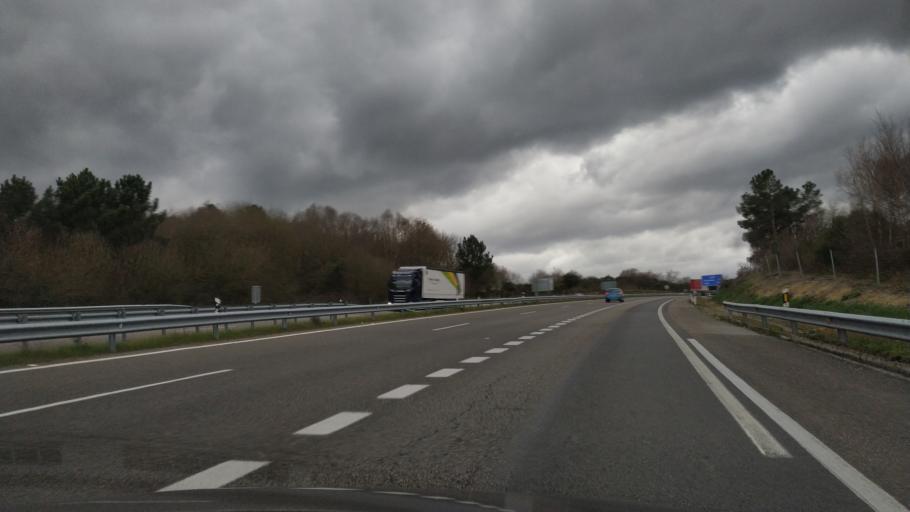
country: ES
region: Galicia
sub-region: Provincia de Ourense
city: Allariz
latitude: 42.2075
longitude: -7.8265
